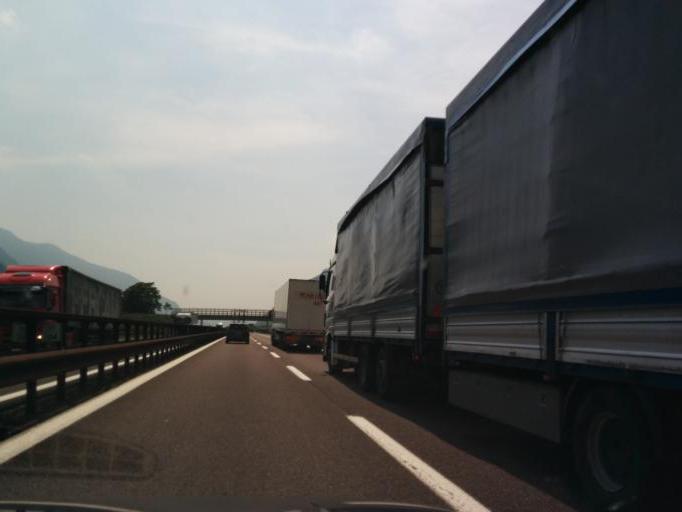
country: IT
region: Veneto
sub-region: Provincia di Verona
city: Rivalta
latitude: 45.6346
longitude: 10.8726
